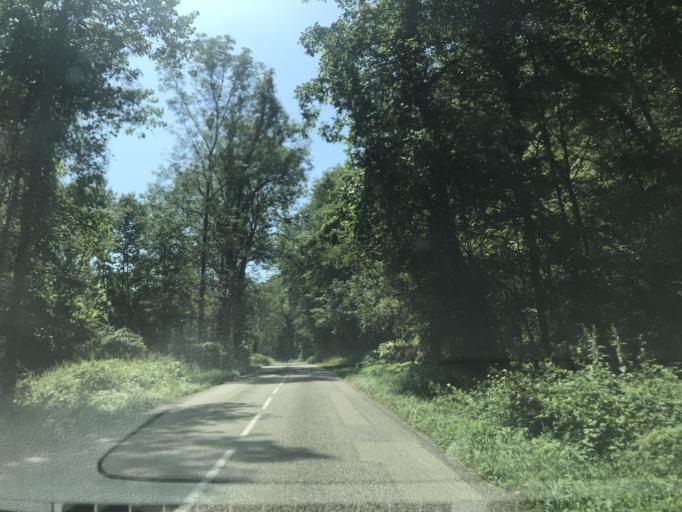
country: FR
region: Rhone-Alpes
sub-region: Departement de la Savoie
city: Chatillon
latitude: 45.8111
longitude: 5.8146
